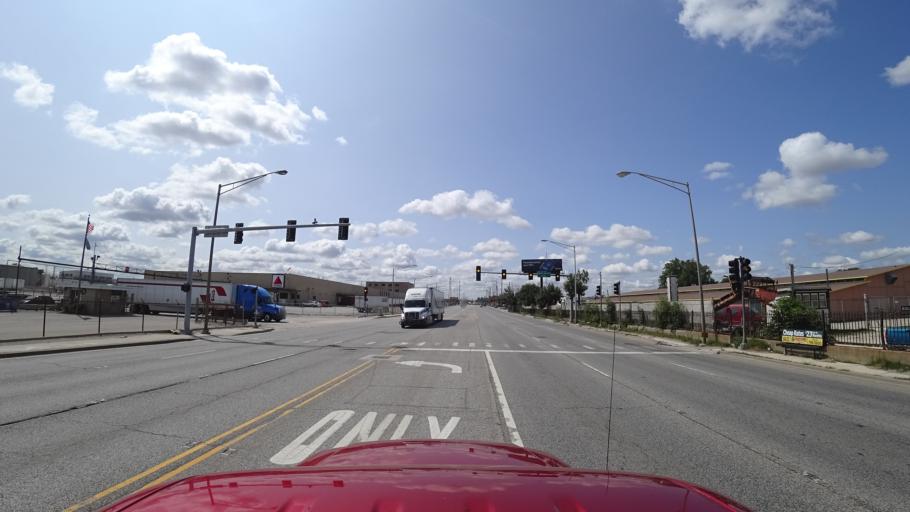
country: US
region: Illinois
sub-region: Cook County
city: Cicero
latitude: 41.8265
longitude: -87.7436
